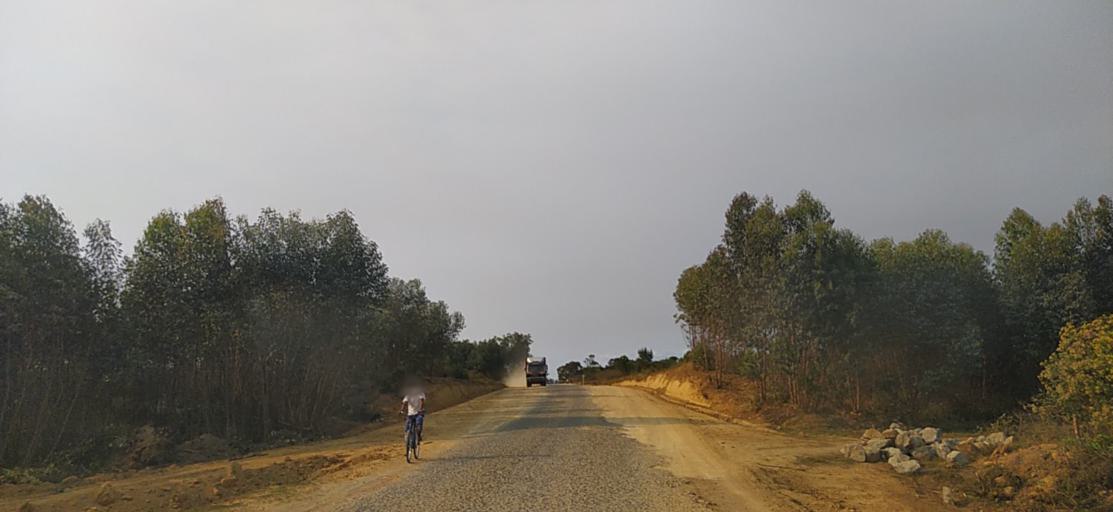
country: MG
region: Alaotra Mangoro
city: Moramanga
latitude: -18.6399
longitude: 48.2757
